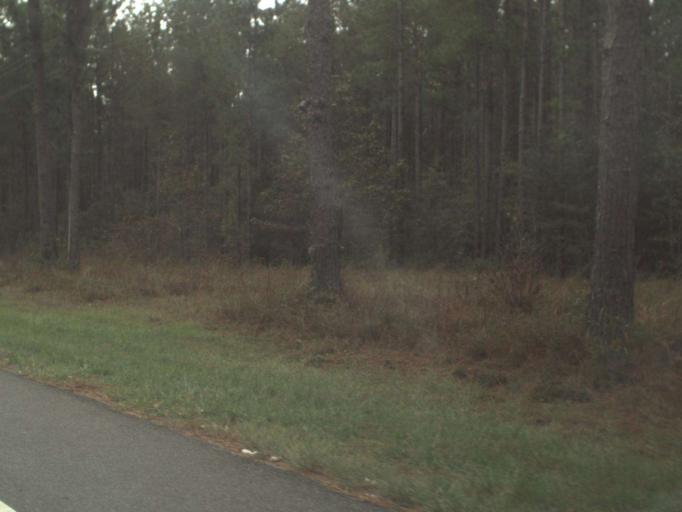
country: US
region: Florida
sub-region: Escambia County
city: Century
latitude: 30.8475
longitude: -87.1475
